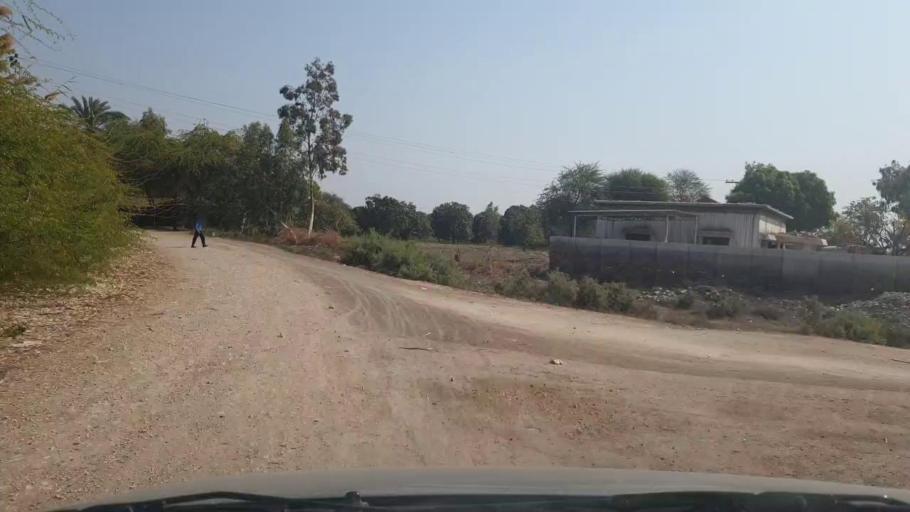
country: PK
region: Sindh
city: Mirwah Gorchani
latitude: 25.2768
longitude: 69.1350
